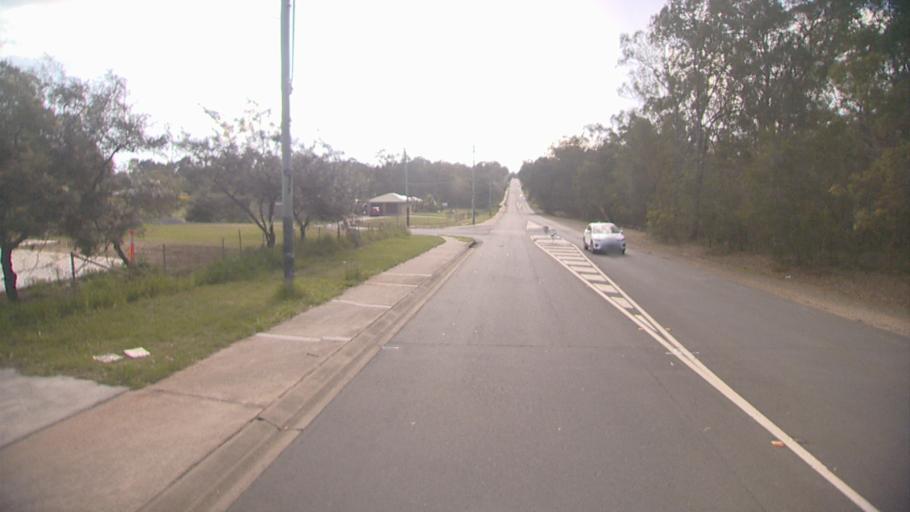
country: AU
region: Queensland
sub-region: Logan
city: Park Ridge South
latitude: -27.6993
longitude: 153.0277
